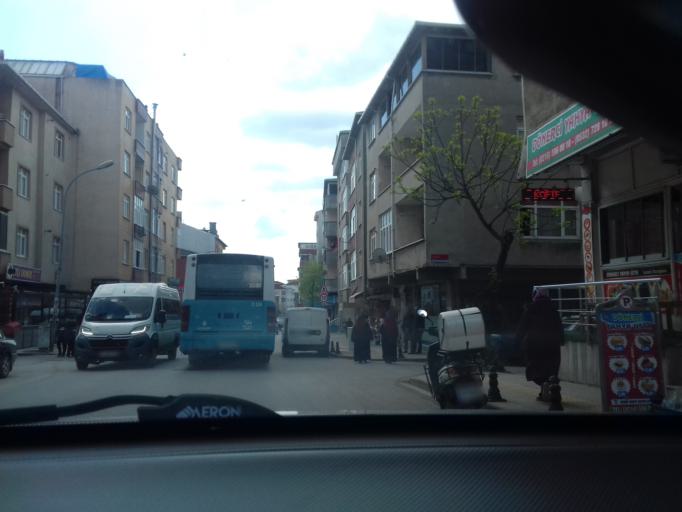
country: TR
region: Istanbul
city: Pendik
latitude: 40.8821
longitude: 29.2867
